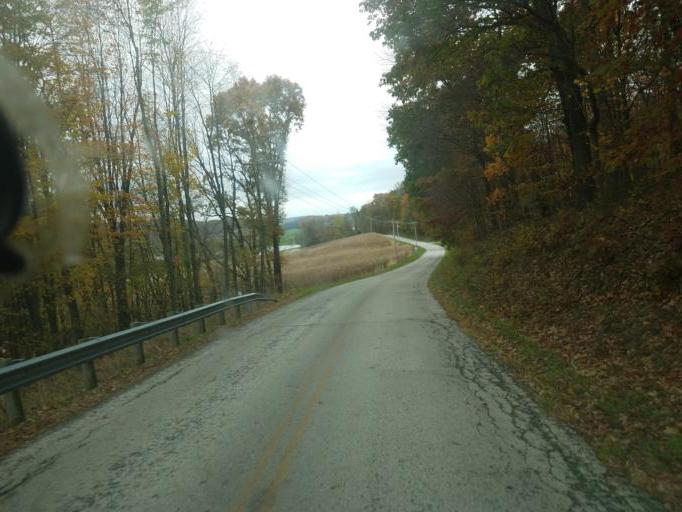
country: US
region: Ohio
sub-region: Ashland County
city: Loudonville
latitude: 40.6229
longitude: -82.1661
